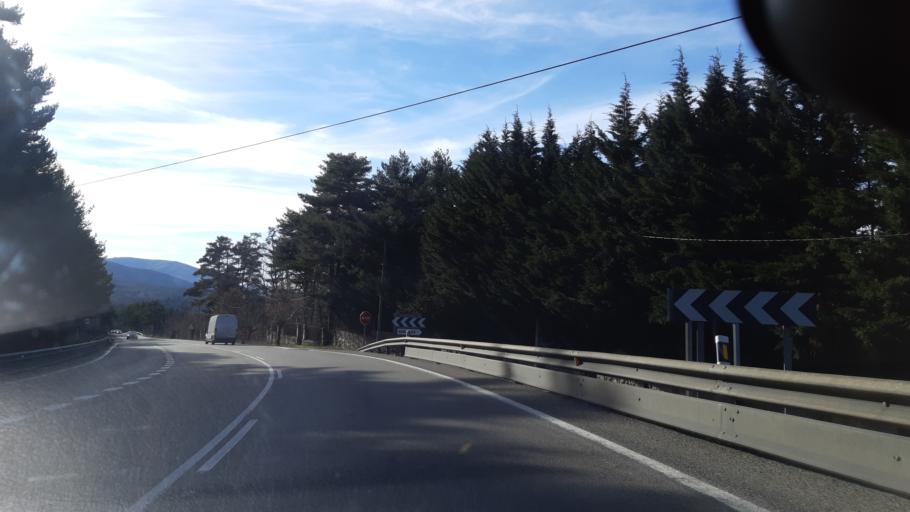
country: ES
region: Madrid
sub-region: Provincia de Madrid
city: Guadarrama
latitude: 40.7126
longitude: -4.1605
